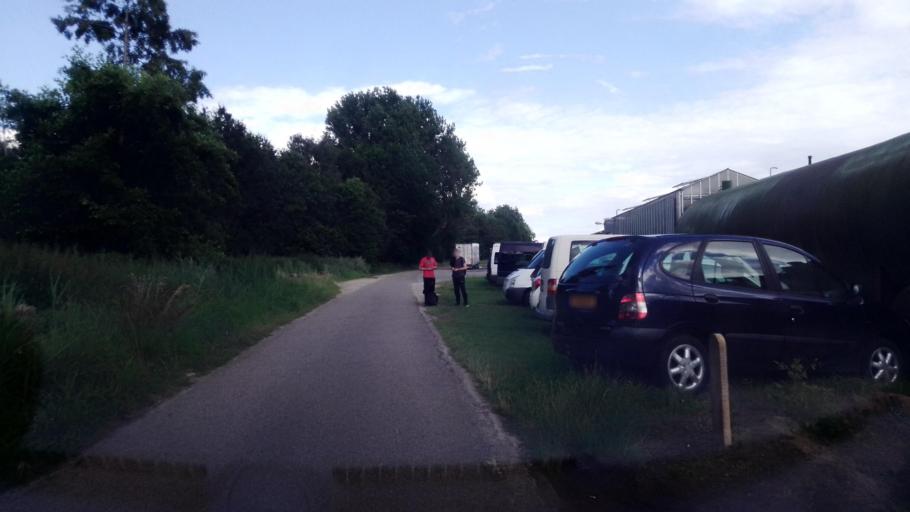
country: NL
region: Limburg
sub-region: Gemeente Venlo
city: Tegelen
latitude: 51.3615
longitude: 6.1036
